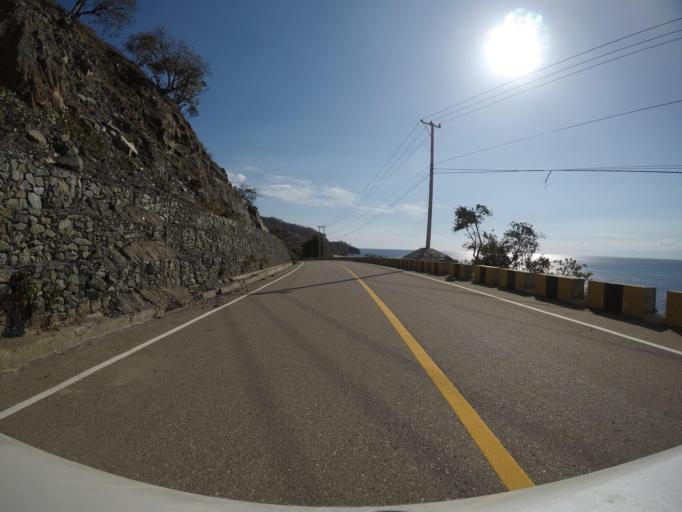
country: TL
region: Liquica
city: Maubara
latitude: -8.6236
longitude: 125.1670
